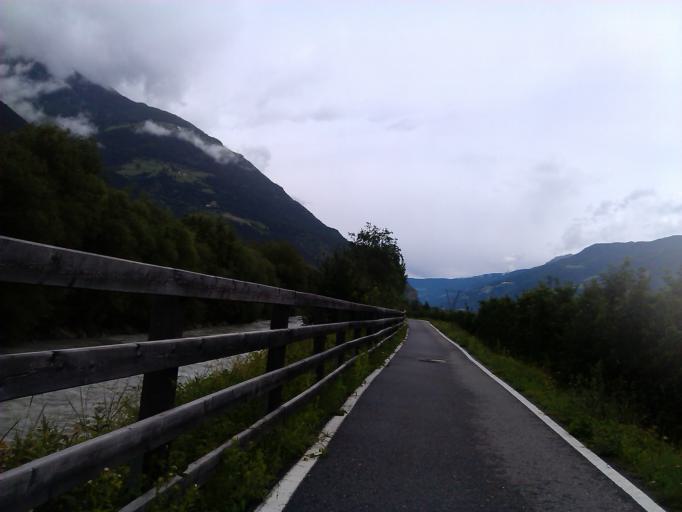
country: IT
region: Trentino-Alto Adige
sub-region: Bolzano
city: Silandro
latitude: 46.6182
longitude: 10.8027
